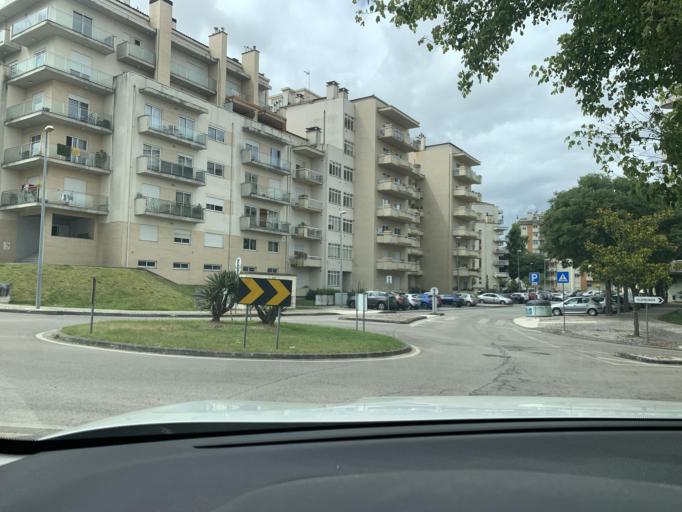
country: PT
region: Viseu
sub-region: Viseu
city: Viseu
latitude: 40.6583
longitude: -7.9265
